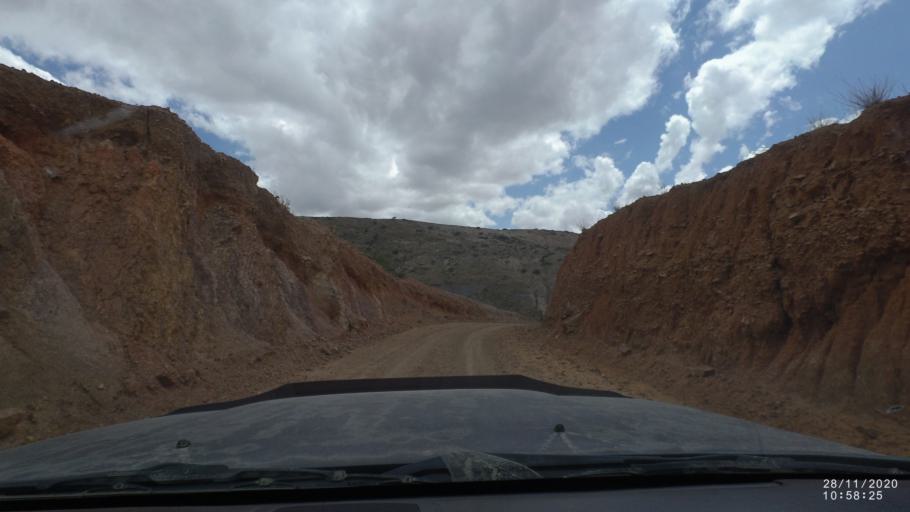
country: BO
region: Cochabamba
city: Capinota
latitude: -17.7750
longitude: -66.1123
